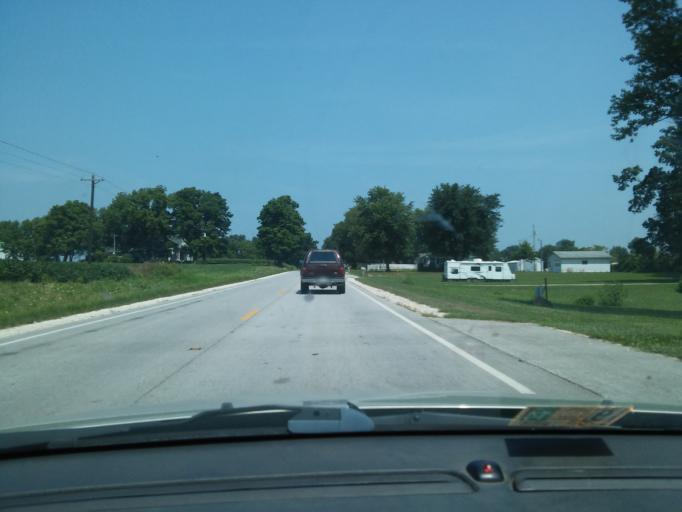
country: US
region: Illinois
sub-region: Pike County
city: Pittsfield
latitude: 39.5415
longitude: -90.9205
